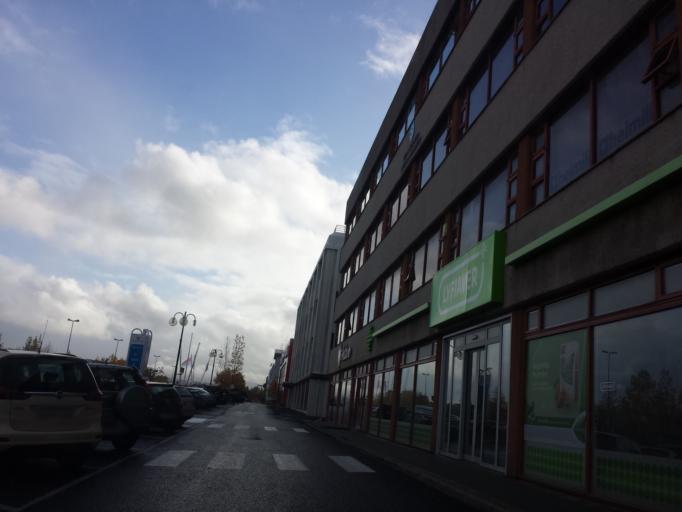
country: IS
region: Capital Region
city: Reykjavik
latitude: 64.1376
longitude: -21.8774
